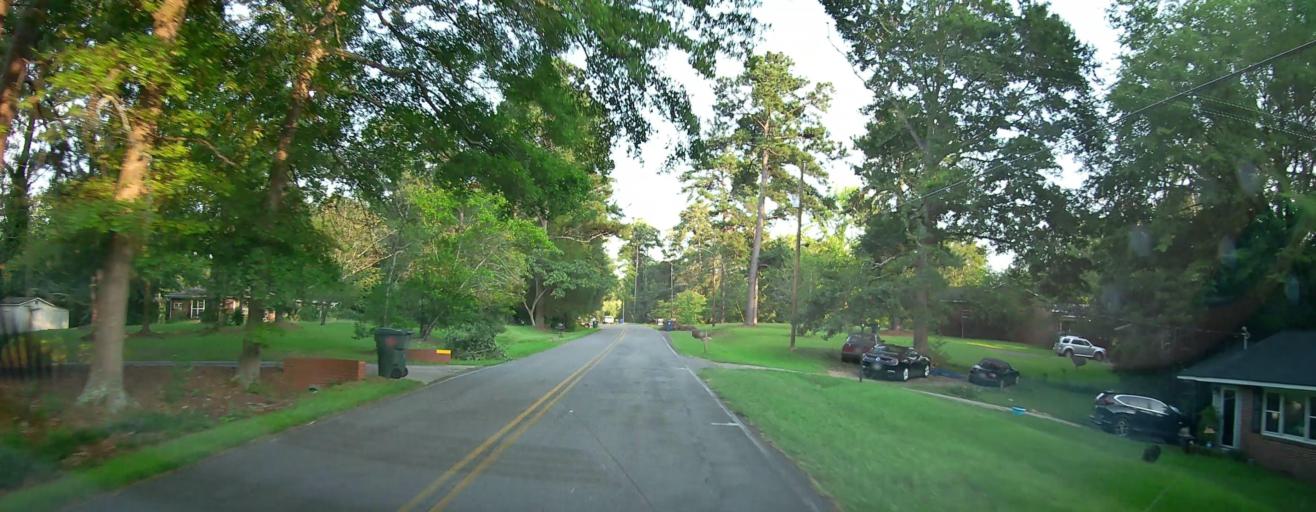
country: US
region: Georgia
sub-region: Bibb County
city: Macon
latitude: 32.8799
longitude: -83.6913
